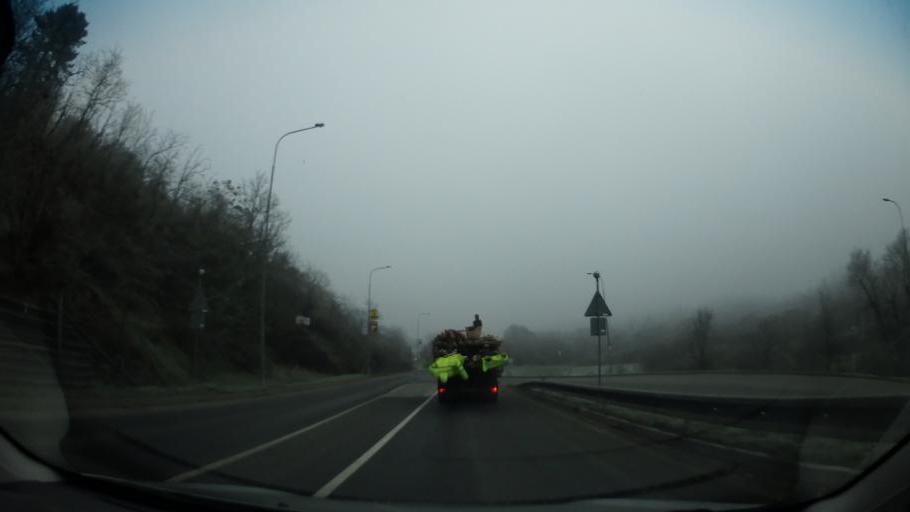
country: CZ
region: Vysocina
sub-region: Okres Trebic
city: Trebic
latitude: 49.2164
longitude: 15.9010
